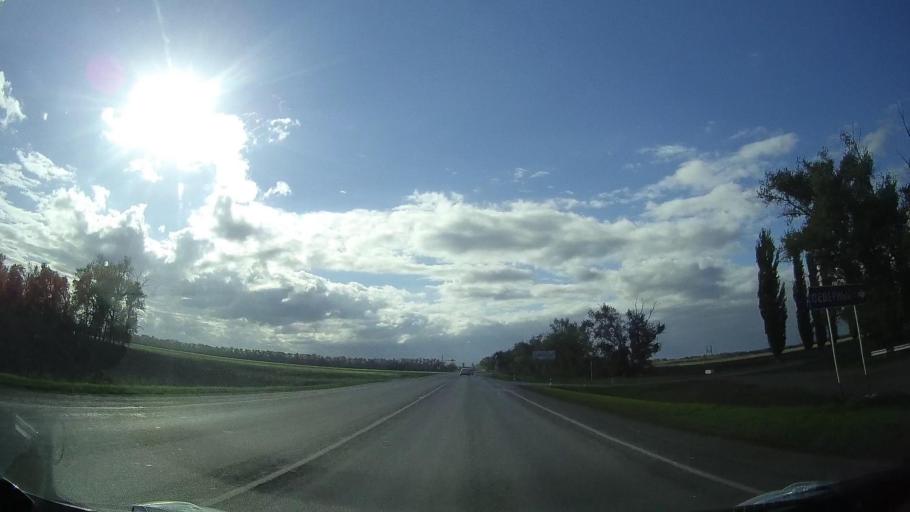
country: RU
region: Rostov
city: Tselina
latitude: 46.5323
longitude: 40.9730
